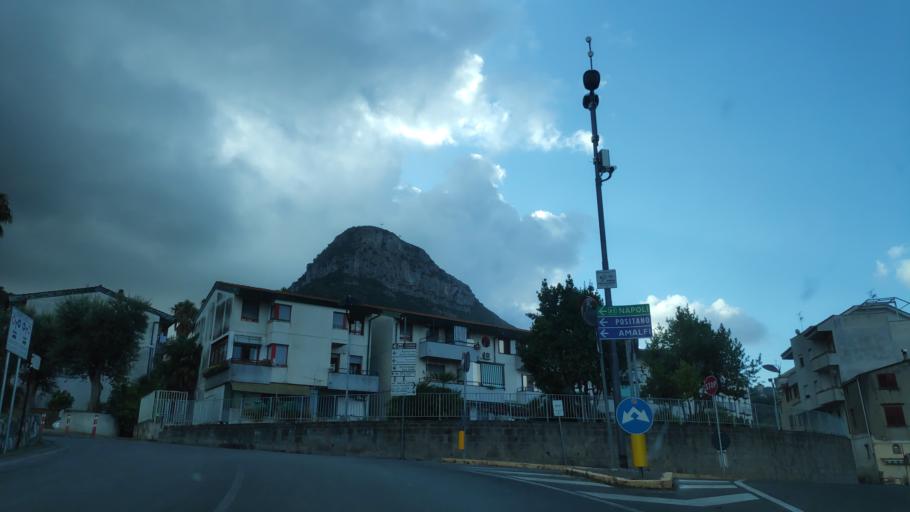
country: IT
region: Campania
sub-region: Provincia di Napoli
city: Piano di Sorrento
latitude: 40.6289
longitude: 14.4217
